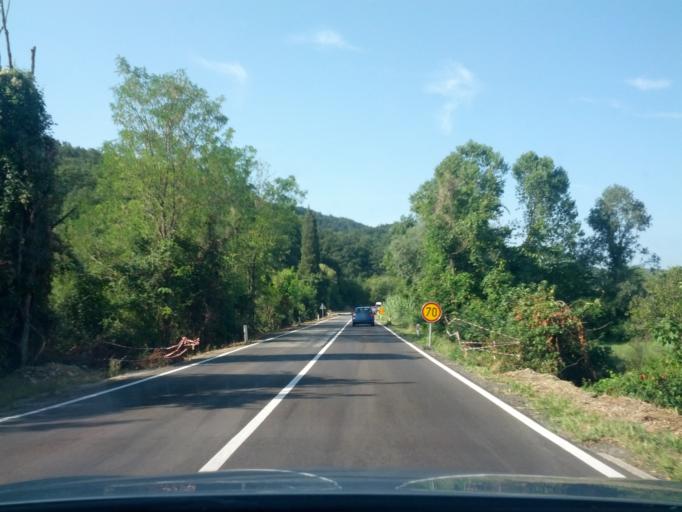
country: SI
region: Izola-Isola
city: Jagodje
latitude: 45.4718
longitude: 13.6726
